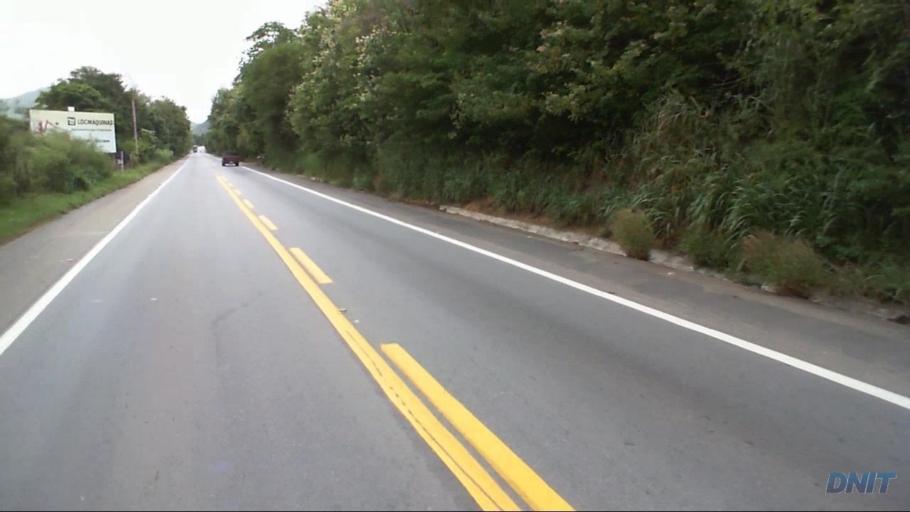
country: BR
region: Minas Gerais
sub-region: Timoteo
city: Timoteo
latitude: -19.5526
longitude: -42.7068
